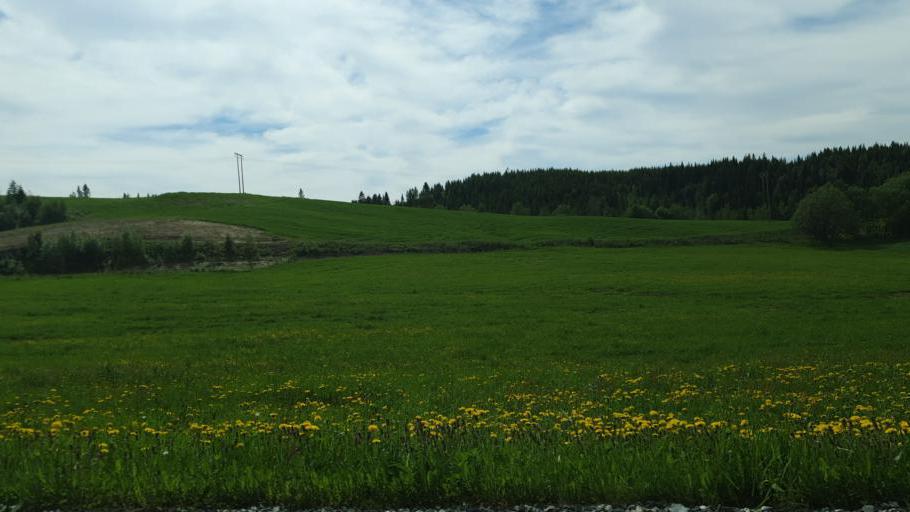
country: NO
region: Nord-Trondelag
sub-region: Leksvik
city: Leksvik
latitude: 63.6868
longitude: 10.5540
